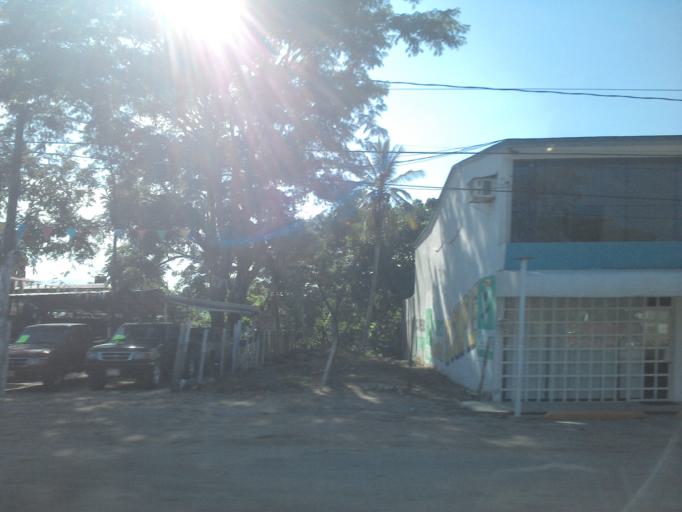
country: MX
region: Chiapas
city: Palenque
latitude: 17.5385
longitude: -91.9914
